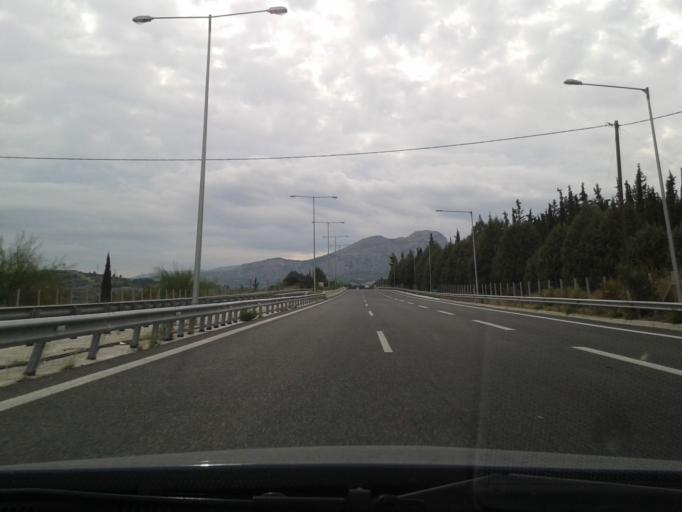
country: GR
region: Peloponnese
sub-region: Nomos Korinthias
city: Arkhaia Korinthos
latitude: 37.8913
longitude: 22.8963
